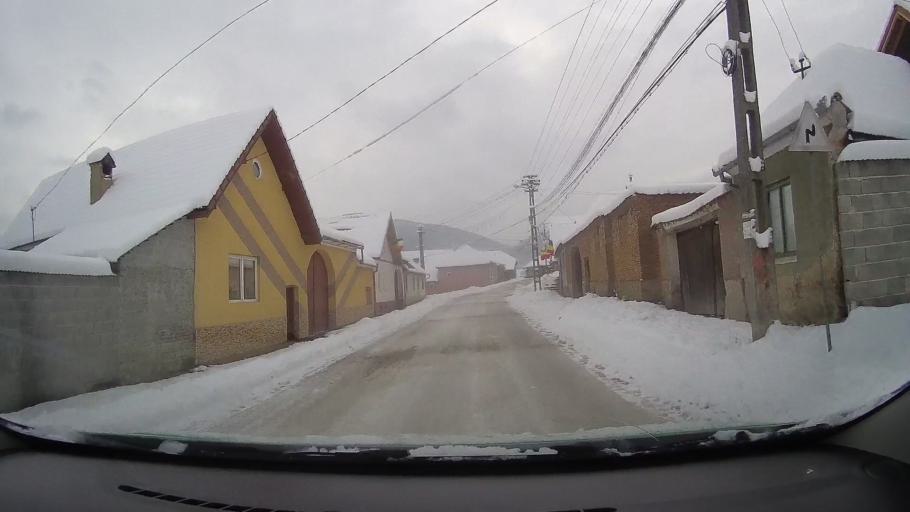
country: RO
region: Alba
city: Pianu de Sus
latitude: 45.8920
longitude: 23.4842
